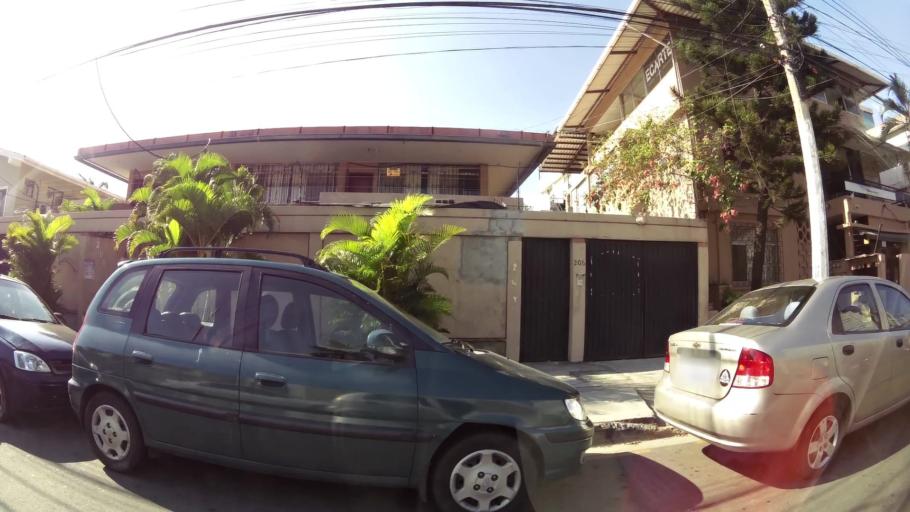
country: EC
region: Guayas
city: Guayaquil
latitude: -2.1748
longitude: -79.9050
